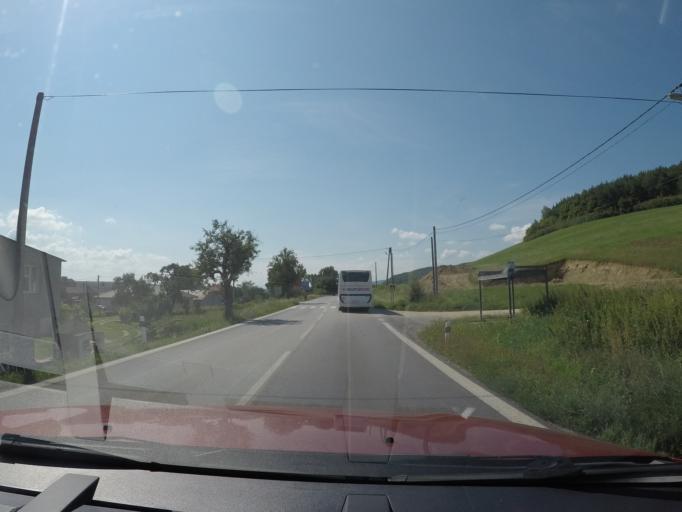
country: SK
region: Presovsky
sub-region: Okres Presov
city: Presov
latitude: 48.9122
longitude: 21.2408
